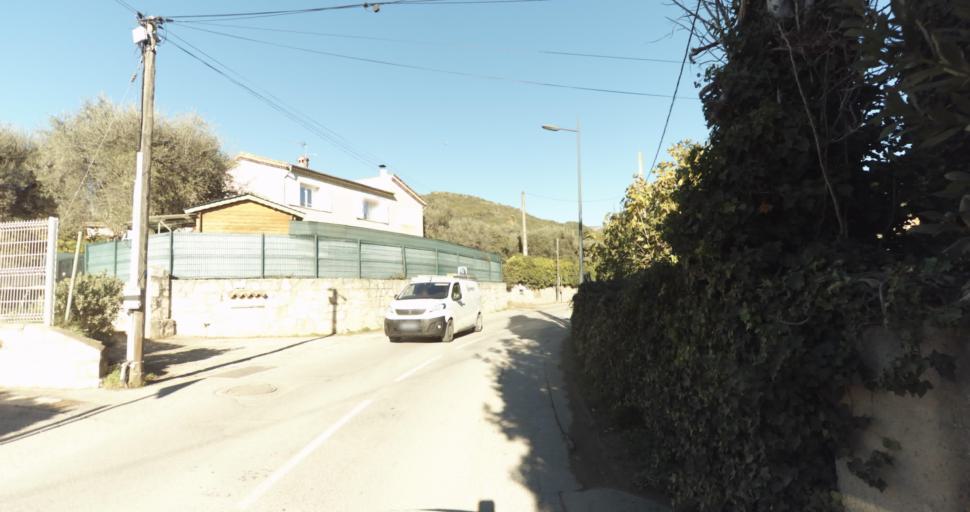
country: FR
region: Provence-Alpes-Cote d'Azur
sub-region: Departement des Alpes-Maritimes
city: Vence
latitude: 43.7182
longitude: 7.0844
